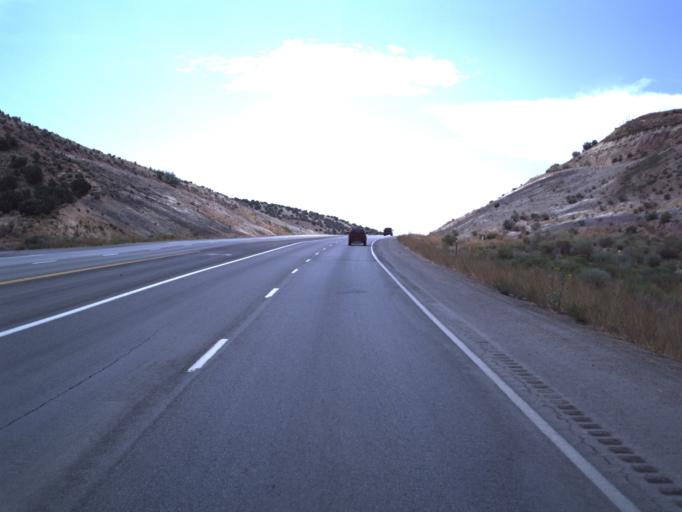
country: US
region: Utah
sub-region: Uintah County
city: Maeser
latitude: 40.4169
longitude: -109.5823
